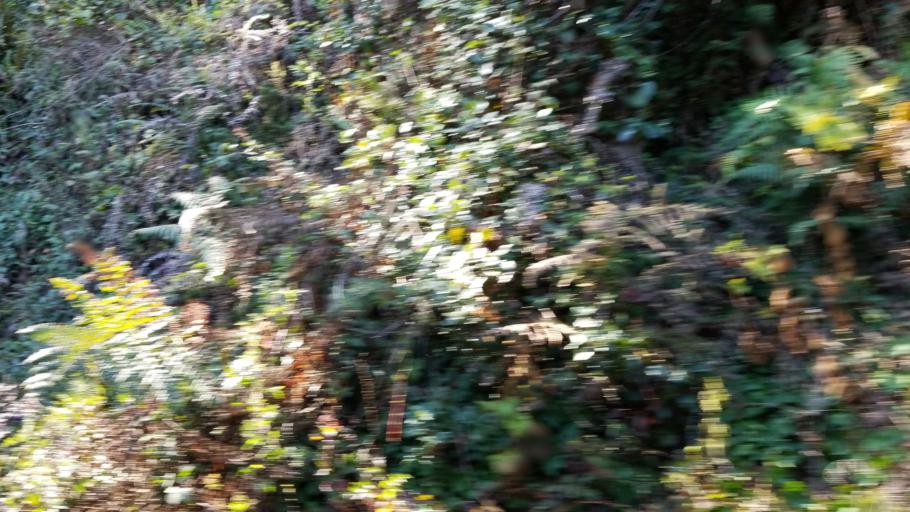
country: US
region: California
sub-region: Mendocino County
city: Fort Bragg
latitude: 39.4469
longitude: -123.7944
